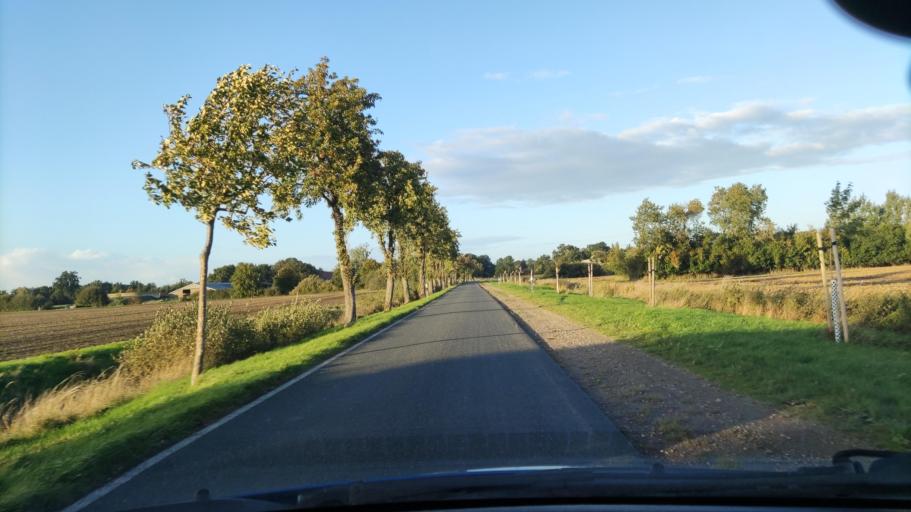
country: DE
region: Lower Saxony
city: Neu Darchau
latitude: 53.2827
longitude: 10.8737
